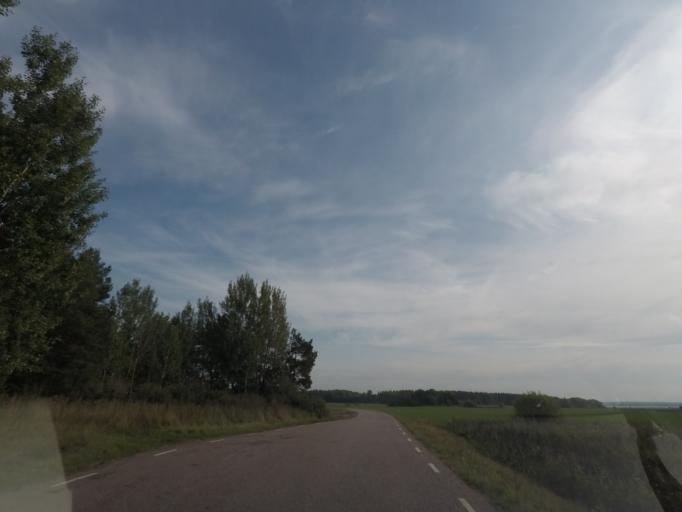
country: SE
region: Vaestmanland
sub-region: Kungsors Kommun
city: Kungsoer
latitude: 59.4932
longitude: 16.1550
